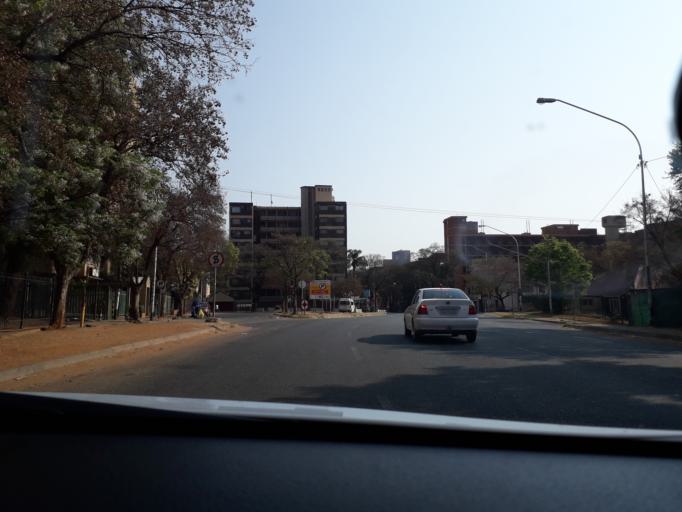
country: ZA
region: Gauteng
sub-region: City of Tshwane Metropolitan Municipality
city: Pretoria
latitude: -25.7575
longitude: 28.1935
